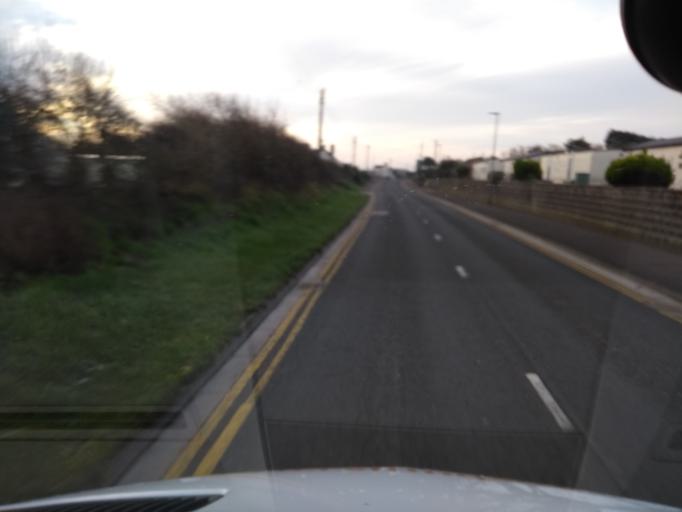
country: GB
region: England
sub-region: Somerset
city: Burnham-on-Sea
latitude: 51.2965
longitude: -3.0103
